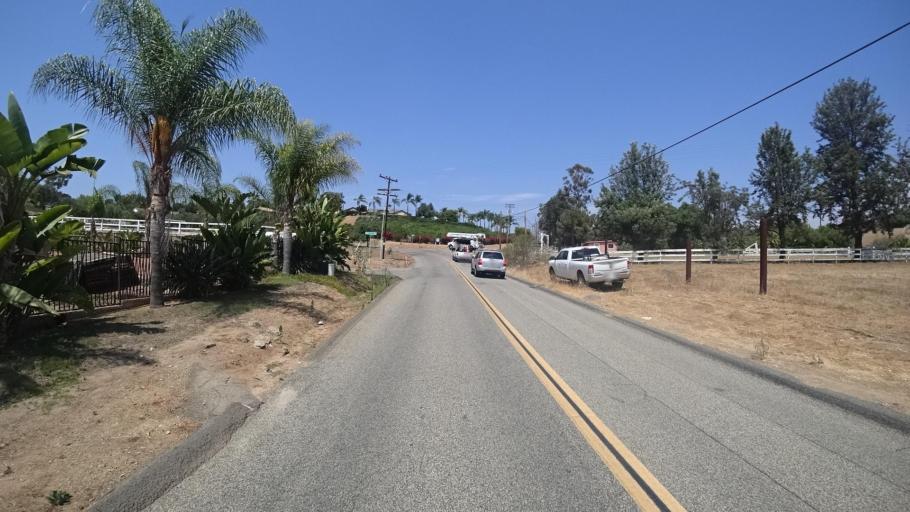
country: US
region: California
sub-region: San Diego County
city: Bonsall
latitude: 33.3132
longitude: -117.2062
